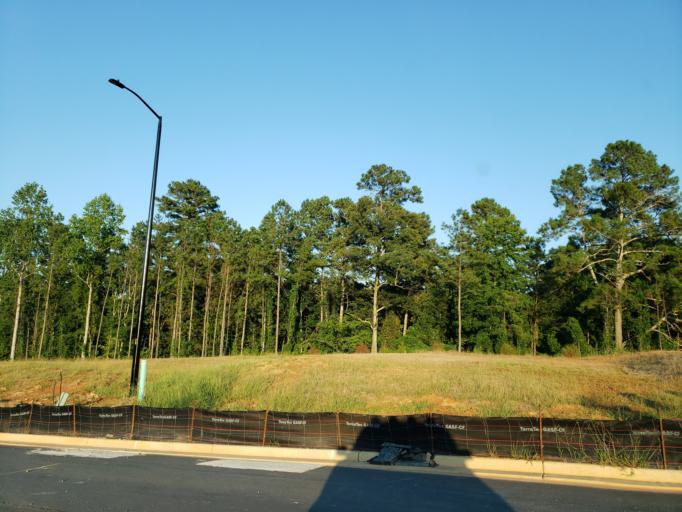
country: US
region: Georgia
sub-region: Paulding County
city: Dallas
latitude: 33.9902
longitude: -84.7695
